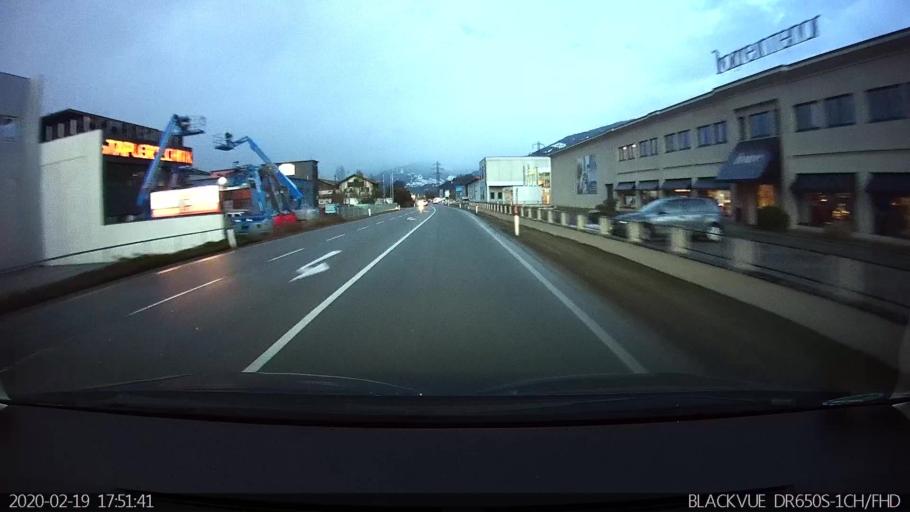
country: AT
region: Tyrol
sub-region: Politischer Bezirk Innsbruck Land
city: Volders
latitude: 47.2832
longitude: 11.5471
